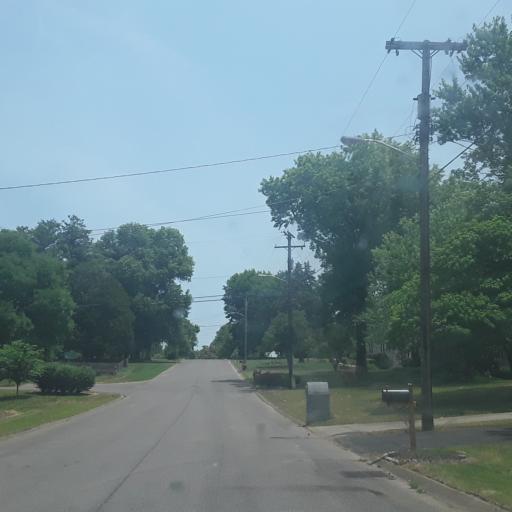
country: US
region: Tennessee
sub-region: Williamson County
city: Brentwood
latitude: 36.0549
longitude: -86.7588
